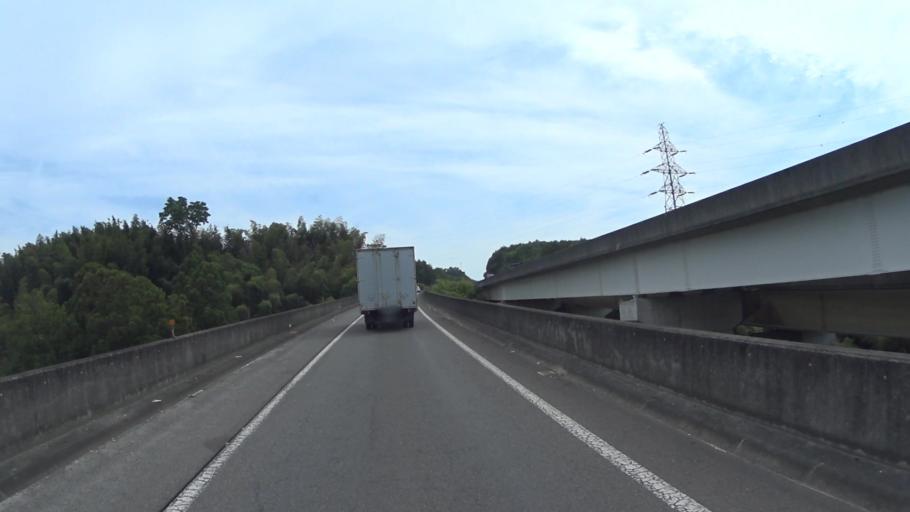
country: JP
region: Shiga Prefecture
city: Kitahama
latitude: 35.1327
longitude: 135.9035
